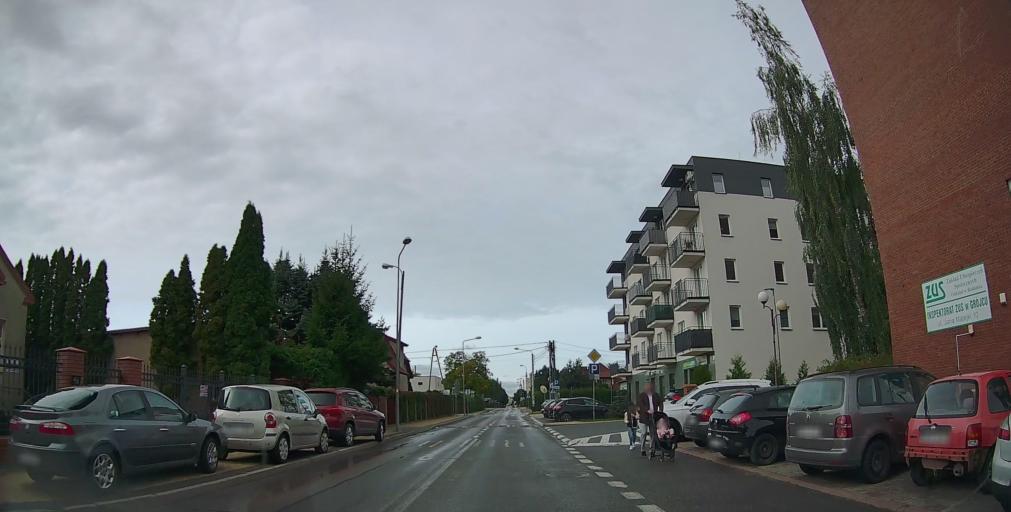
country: PL
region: Masovian Voivodeship
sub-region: Powiat grojecki
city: Grojec
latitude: 51.8698
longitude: 20.8840
